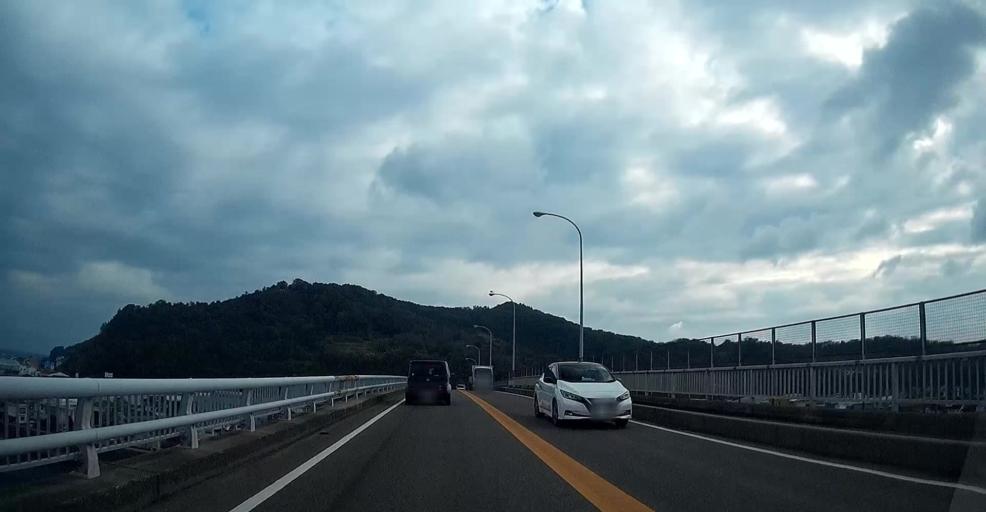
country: JP
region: Kumamoto
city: Hondo
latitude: 32.4477
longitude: 130.2049
